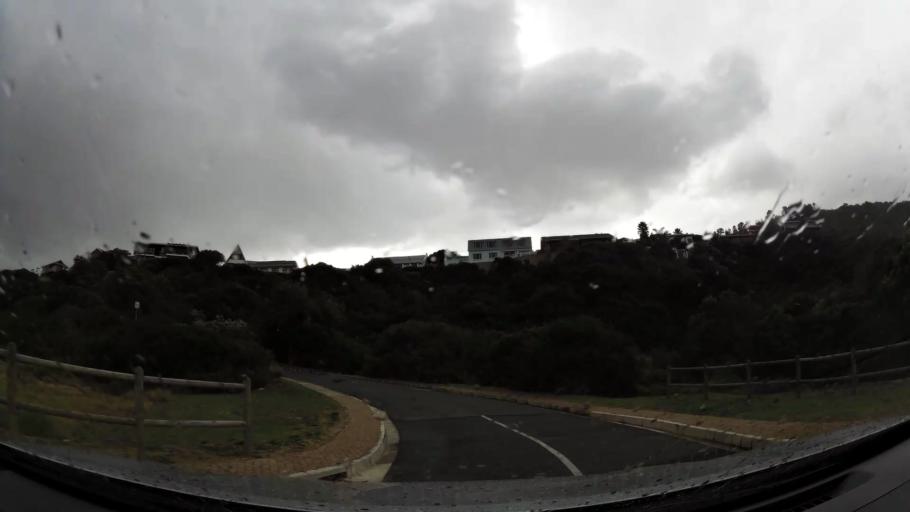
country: ZA
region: Western Cape
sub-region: Eden District Municipality
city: George
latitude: -34.0492
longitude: 22.2963
